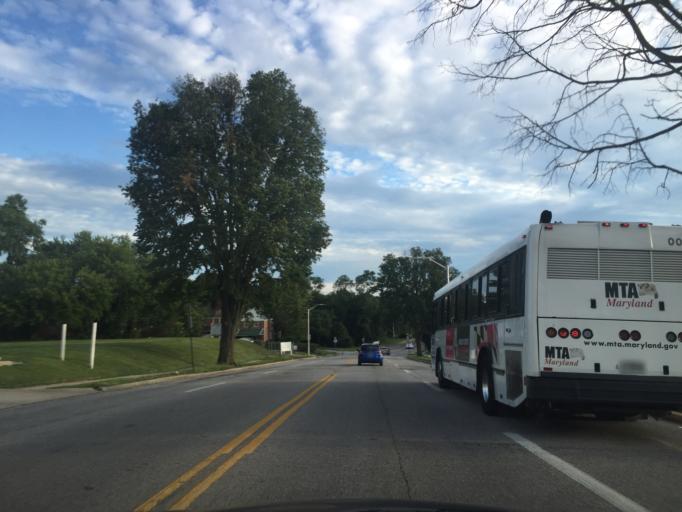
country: US
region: Maryland
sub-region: Baltimore County
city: Towson
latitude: 39.3580
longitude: -76.5951
